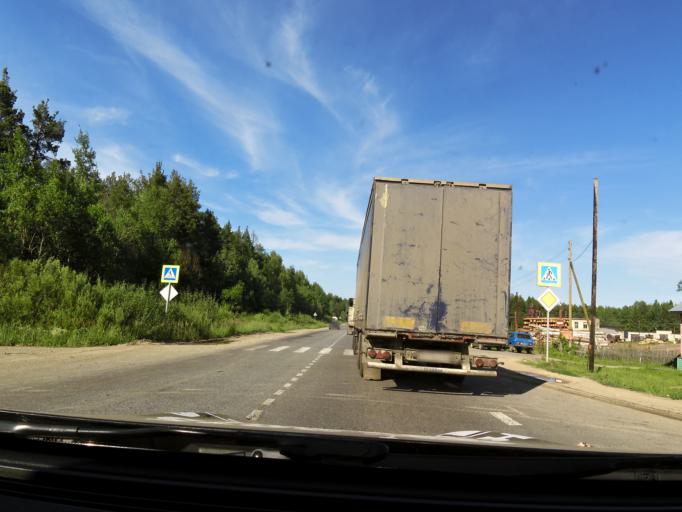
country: RU
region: Kirov
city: Belaya Kholunitsa
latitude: 58.8705
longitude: 50.8456
